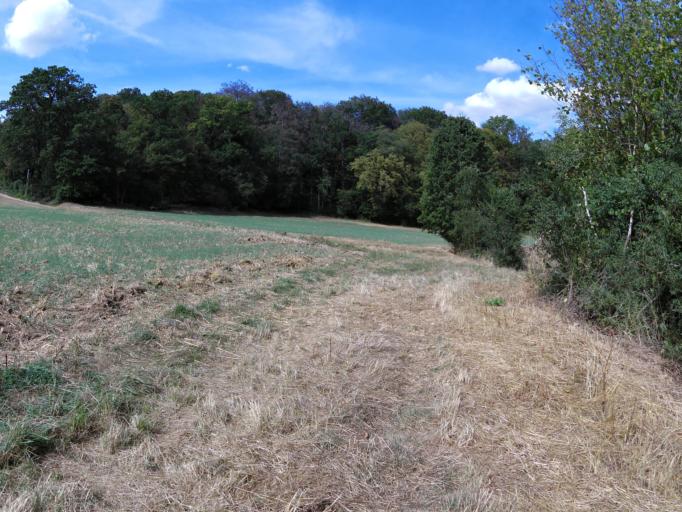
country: DE
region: Bavaria
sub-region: Regierungsbezirk Unterfranken
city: Guntersleben
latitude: 49.8601
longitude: 9.9223
